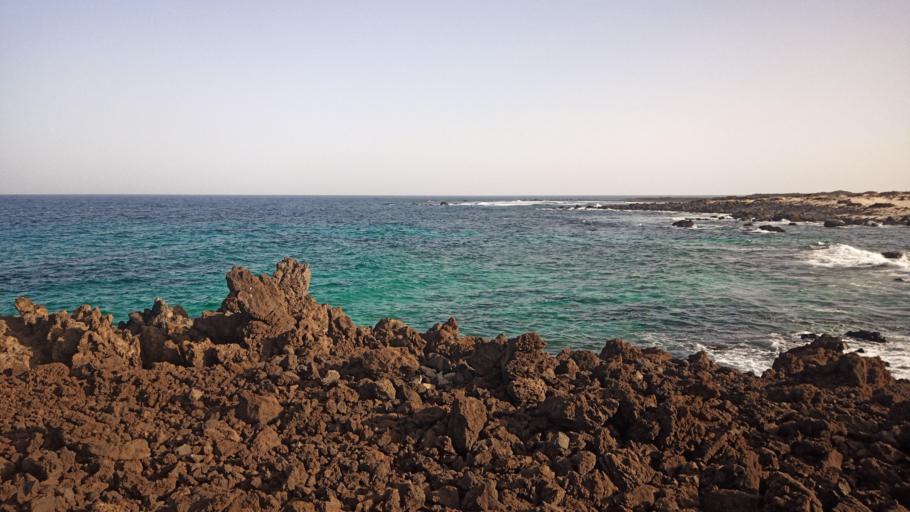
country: ES
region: Canary Islands
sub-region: Provincia de Las Palmas
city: Haria
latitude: 29.2069
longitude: -13.4242
